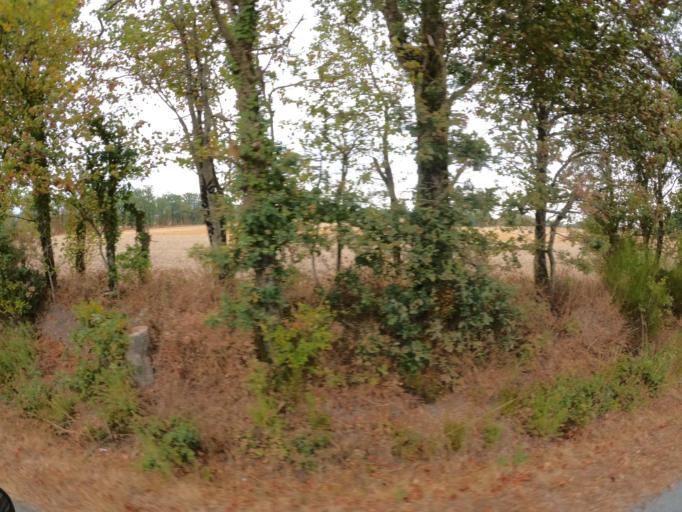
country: FR
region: Pays de la Loire
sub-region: Departement de la Vendee
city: Treize-Septiers
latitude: 46.9778
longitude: -1.2010
